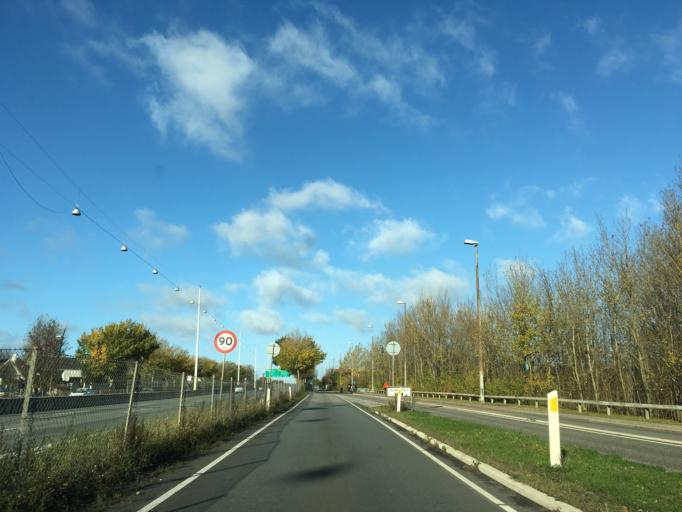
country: DK
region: Capital Region
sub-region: Lyngby-Tarbaek Kommune
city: Kongens Lyngby
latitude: 55.7479
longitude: 12.5292
